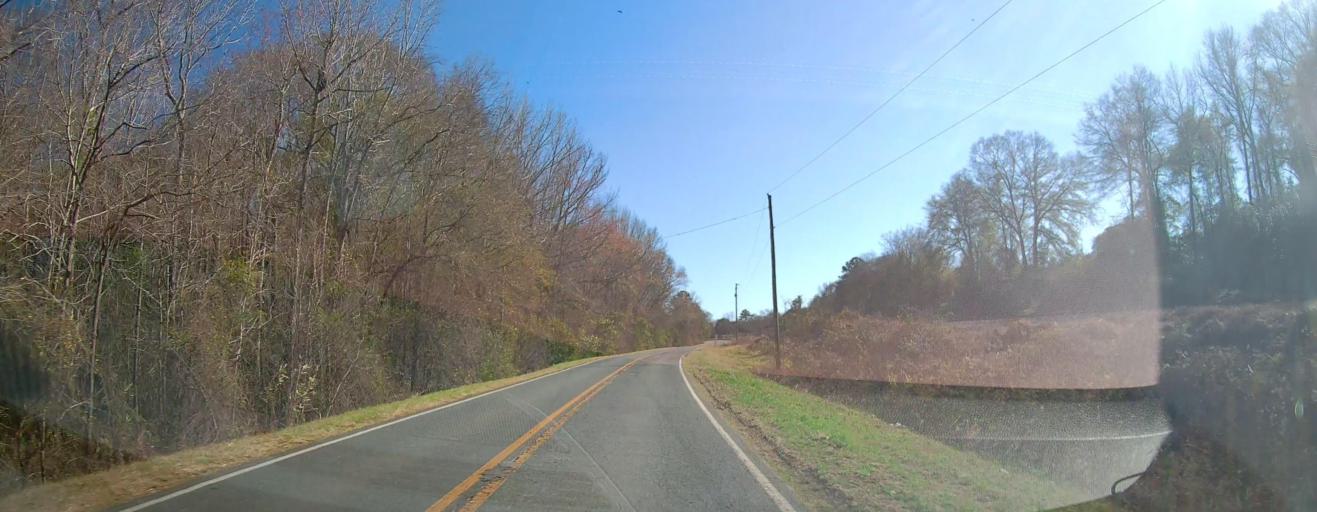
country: US
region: Georgia
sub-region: Macon County
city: Oglethorpe
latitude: 32.3066
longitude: -84.0637
